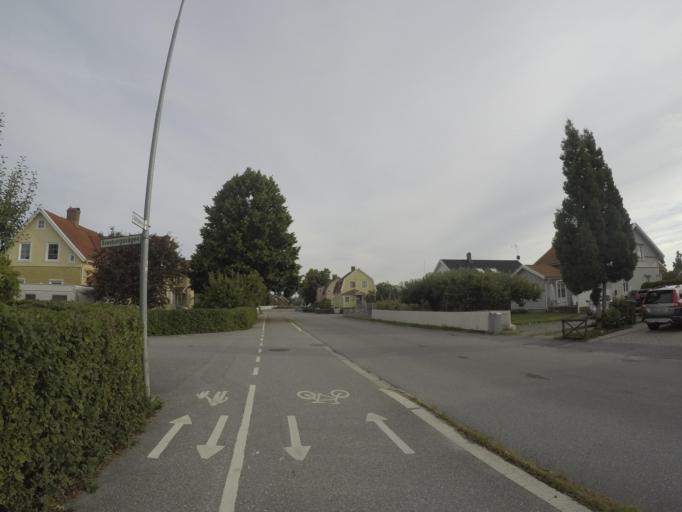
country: SE
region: OErebro
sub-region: Orebro Kommun
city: Orebro
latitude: 59.2606
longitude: 15.2485
